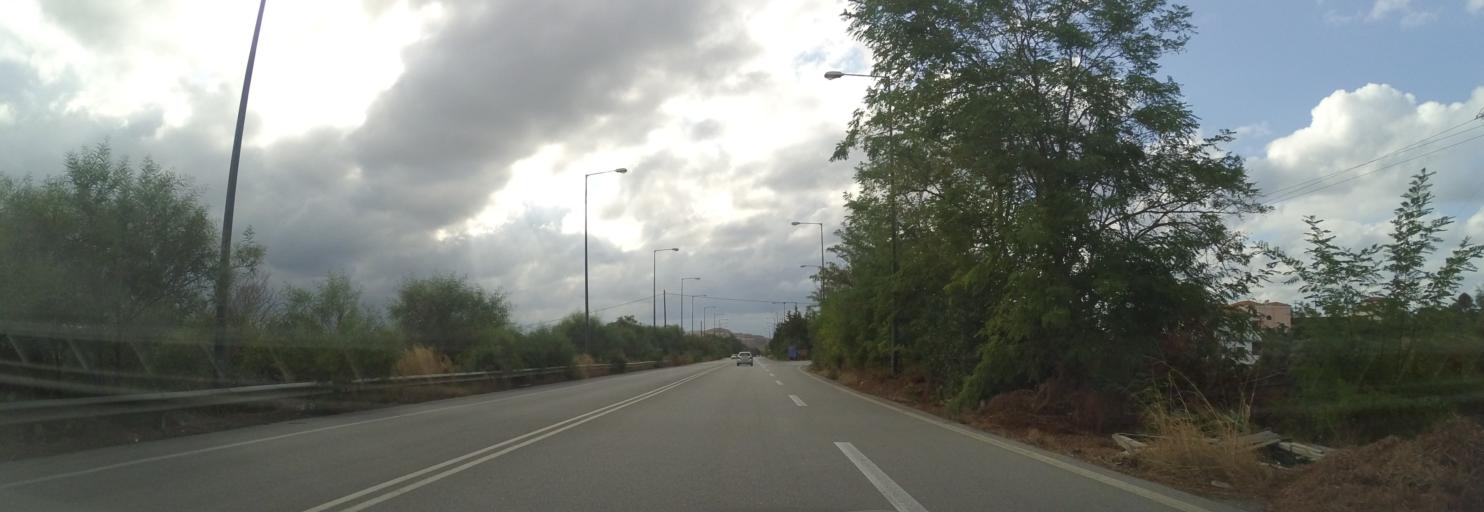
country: GR
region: Crete
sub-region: Nomos Rethymnis
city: Panormos
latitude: 35.4149
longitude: 24.6999
